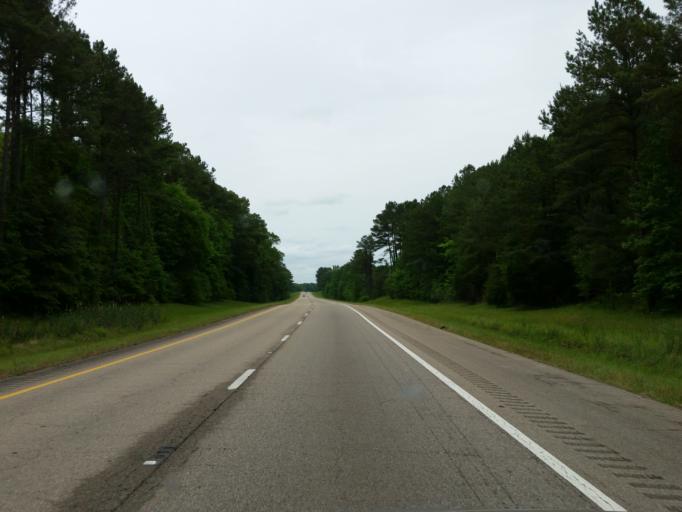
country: US
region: Mississippi
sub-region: Clarke County
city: Stonewall
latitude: 31.9806
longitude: -88.9514
